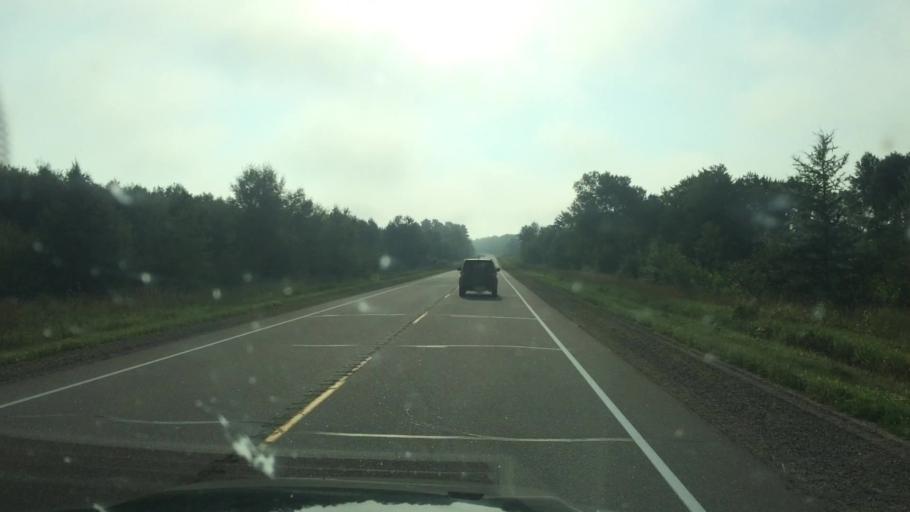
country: US
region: Wisconsin
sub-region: Langlade County
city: Antigo
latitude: 45.1450
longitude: -89.3137
